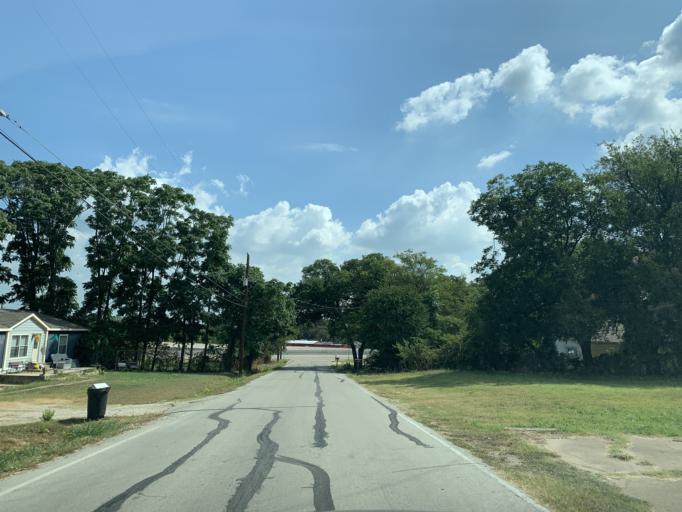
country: US
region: Texas
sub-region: Tarrant County
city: Azle
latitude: 32.8682
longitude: -97.5260
